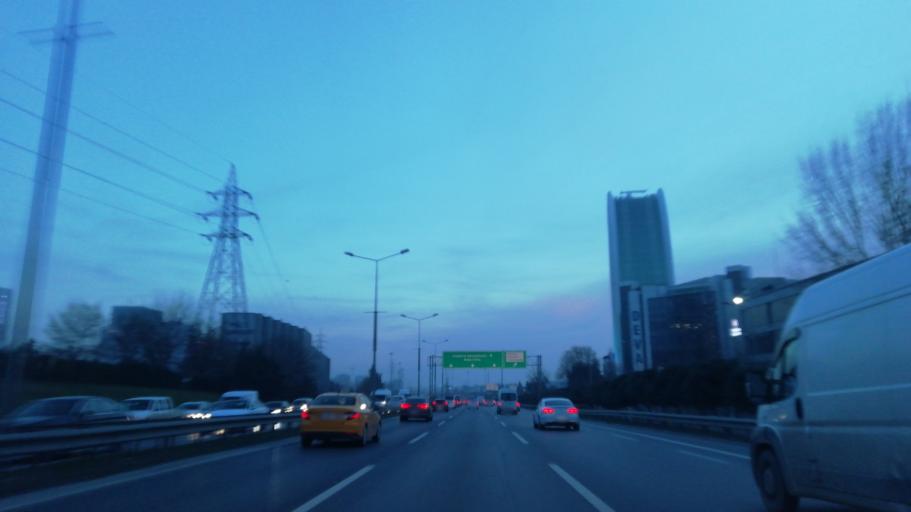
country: TR
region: Istanbul
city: Mahmutbey
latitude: 41.0319
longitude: 28.8107
